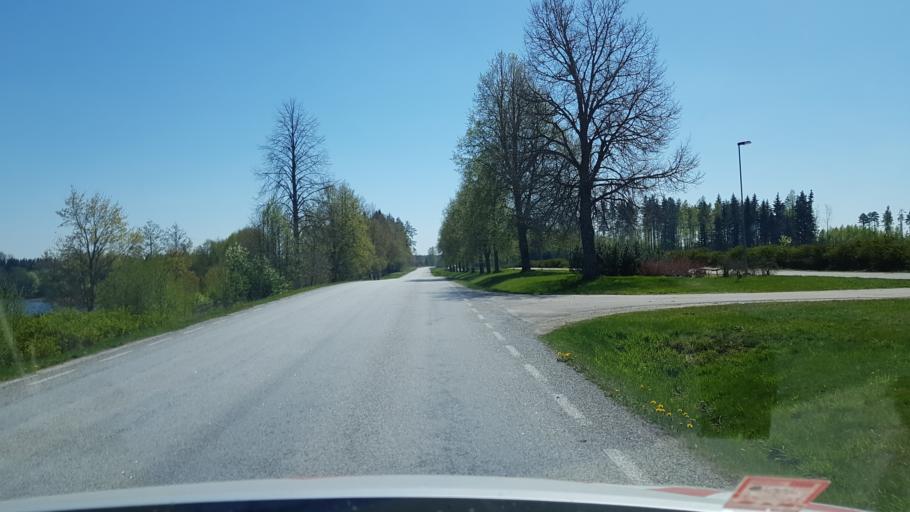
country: EE
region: Vorumaa
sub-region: Voru linn
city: Voru
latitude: 57.8959
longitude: 26.9990
